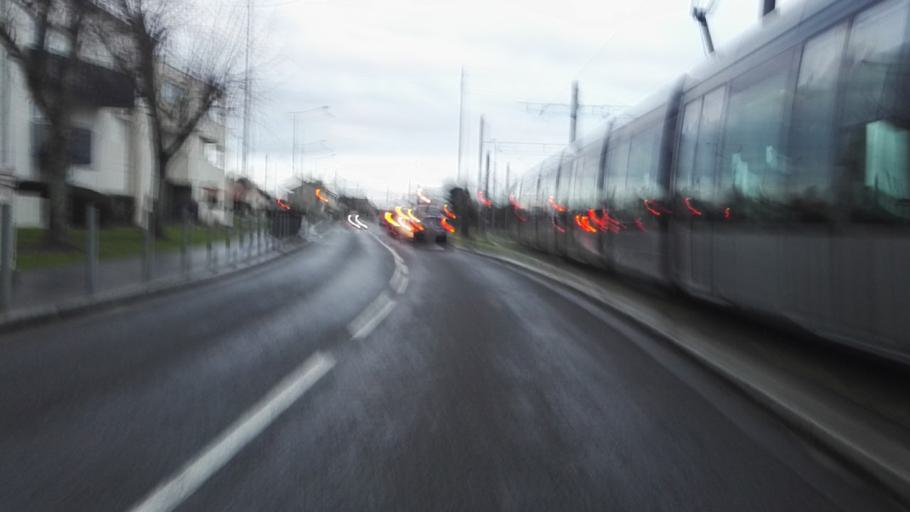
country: FR
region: Aquitaine
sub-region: Departement de la Gironde
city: Merignac
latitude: 44.8290
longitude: -0.6277
